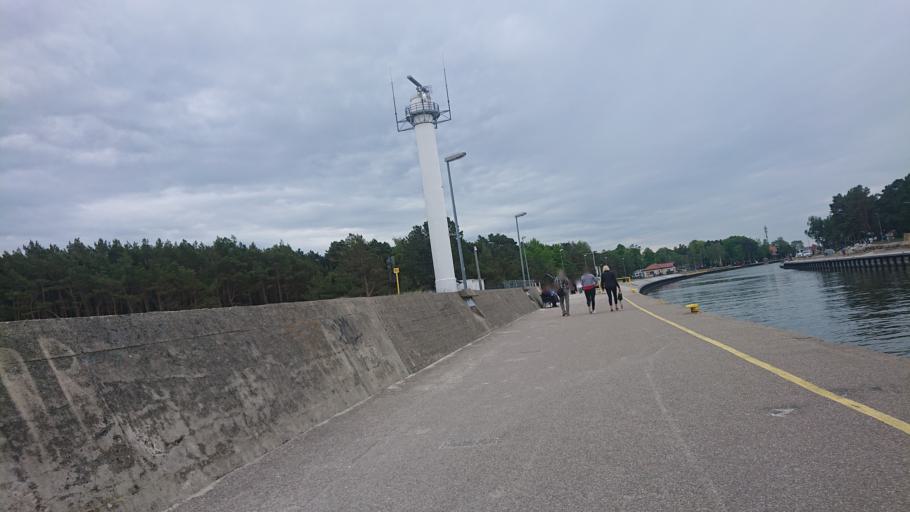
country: PL
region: Pomeranian Voivodeship
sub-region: Powiat leborski
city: Leba
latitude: 54.7679
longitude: 17.5513
